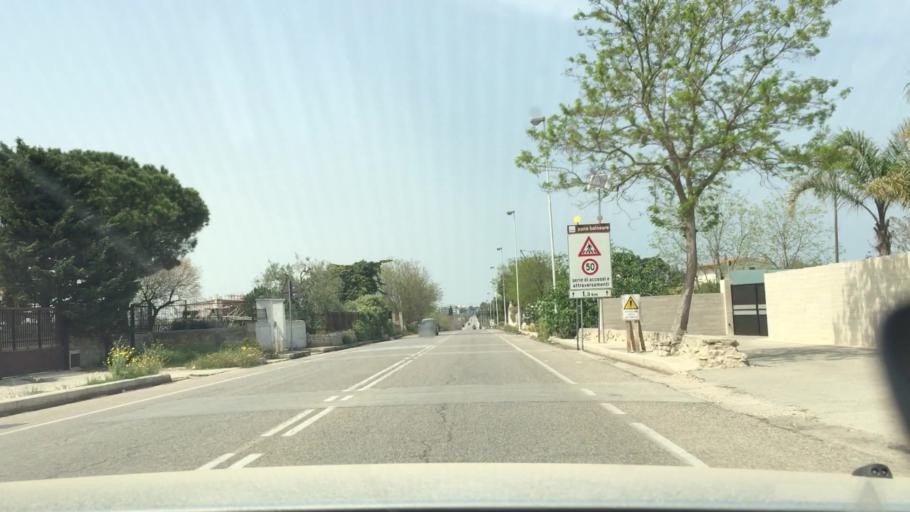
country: IT
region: Apulia
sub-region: Provincia di Barletta - Andria - Trani
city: Capirro
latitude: 41.2572
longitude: 16.4559
